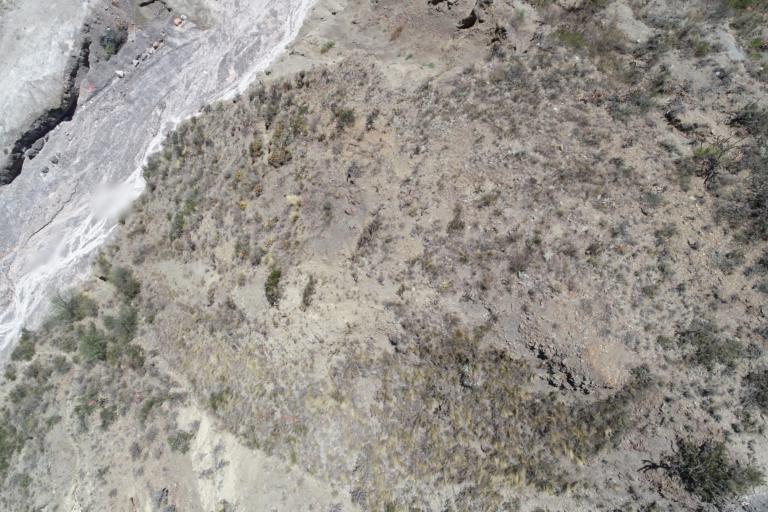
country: BO
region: La Paz
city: La Paz
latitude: -16.6411
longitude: -68.0404
